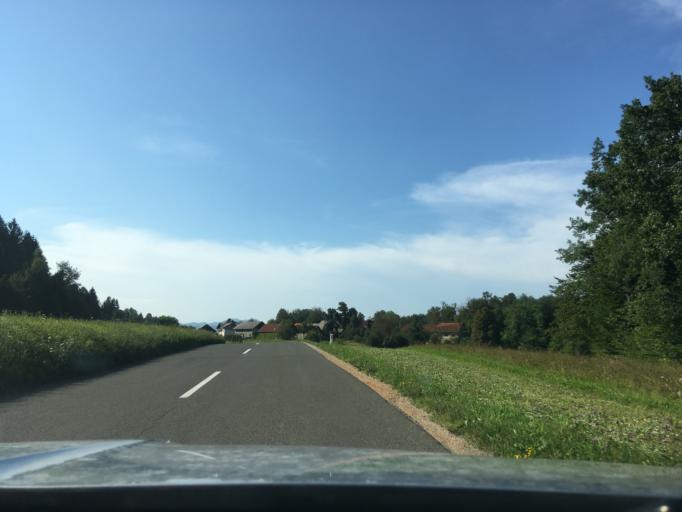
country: SI
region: Crnomelj
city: Crnomelj
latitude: 45.5051
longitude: 15.1899
